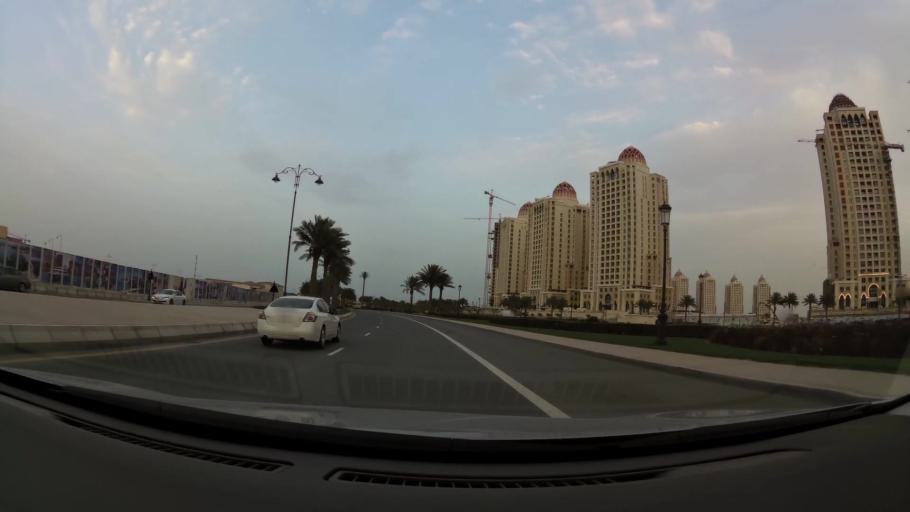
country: QA
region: Baladiyat ad Dawhah
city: Doha
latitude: 25.3710
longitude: 51.5532
